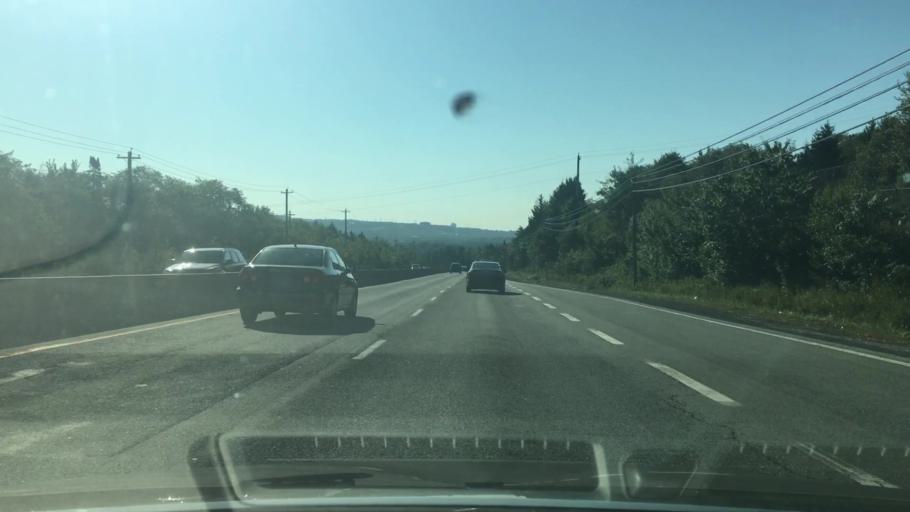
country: CA
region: Nova Scotia
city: Dartmouth
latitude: 44.7119
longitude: -63.6281
